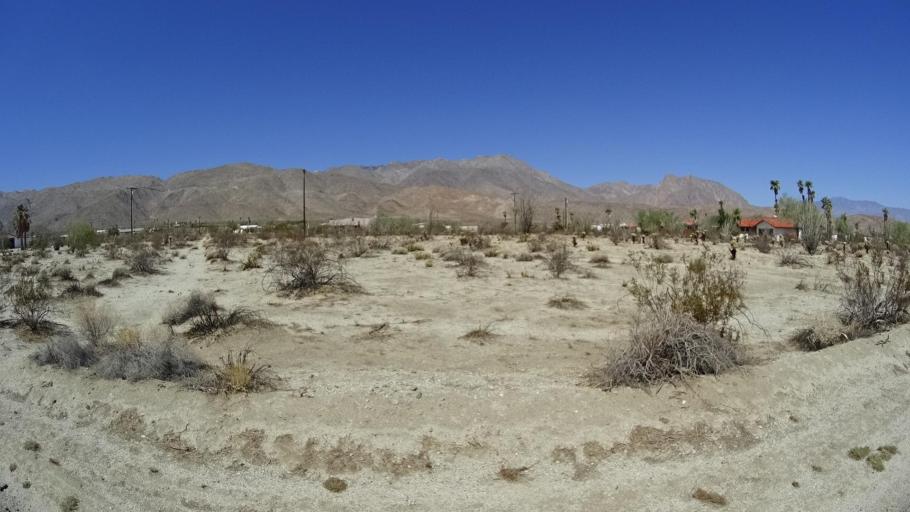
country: US
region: California
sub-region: San Diego County
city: Borrego Springs
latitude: 33.2276
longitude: -116.3855
